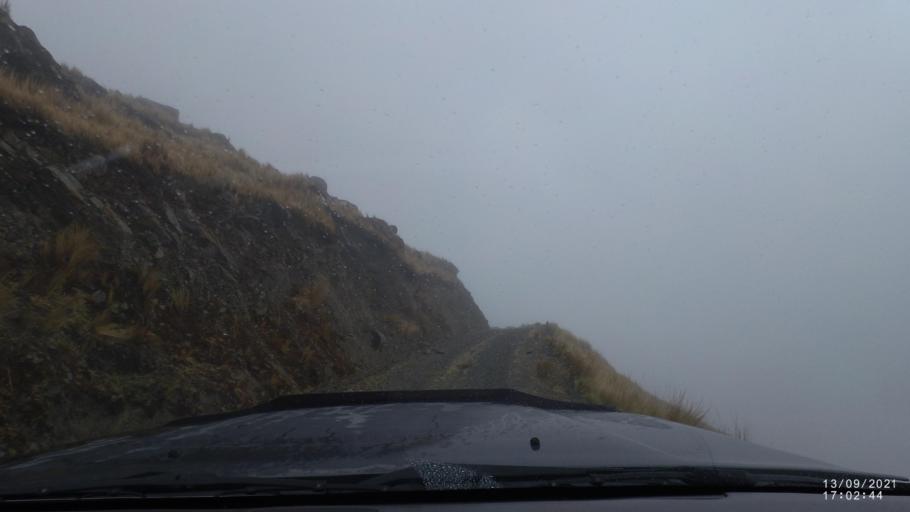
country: BO
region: Cochabamba
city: Colomi
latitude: -17.3189
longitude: -65.7228
